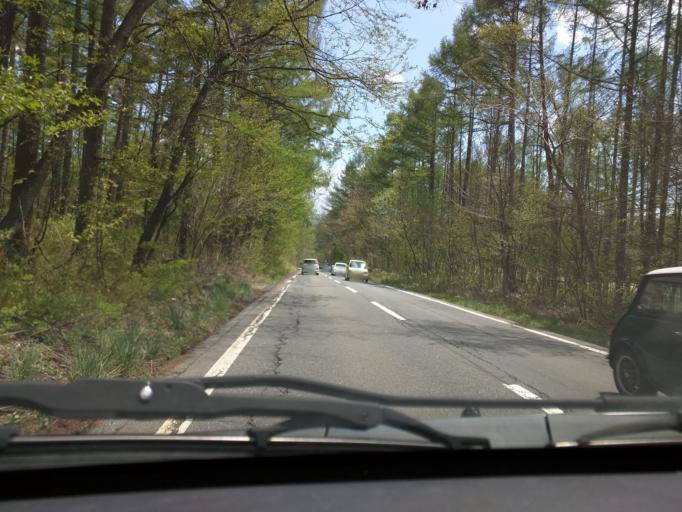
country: JP
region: Nagano
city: Nagano-shi
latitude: 36.7094
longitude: 138.1294
